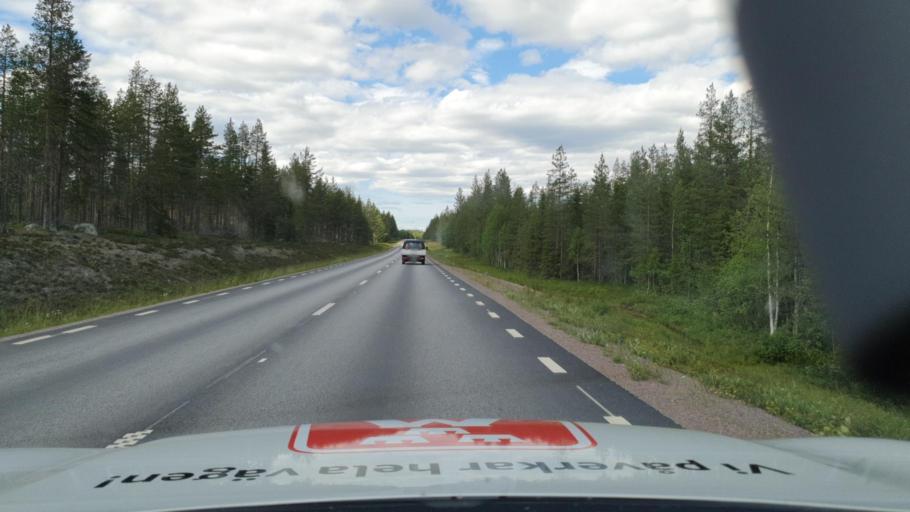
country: SE
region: Vaesterbotten
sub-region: Skelleftea Kommun
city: Langsele
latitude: 65.0894
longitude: 19.9975
